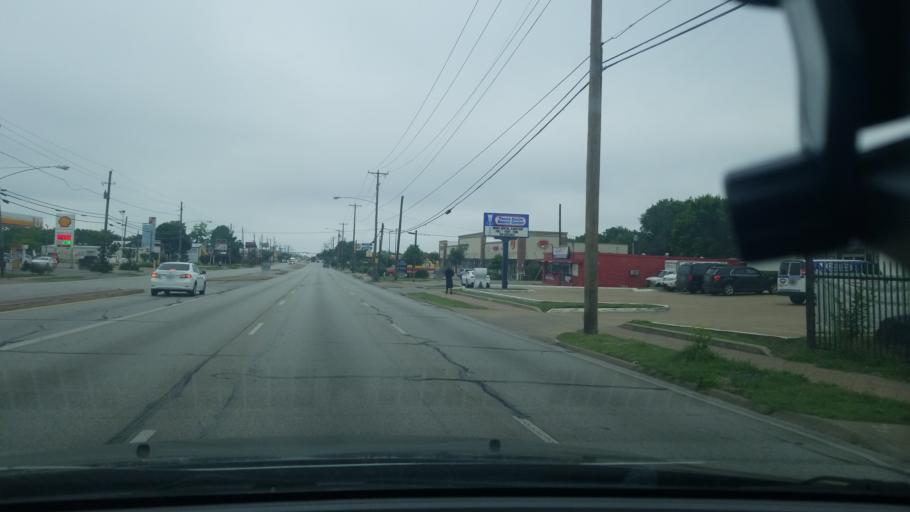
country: US
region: Texas
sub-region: Dallas County
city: Balch Springs
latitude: 32.7555
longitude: -96.6829
